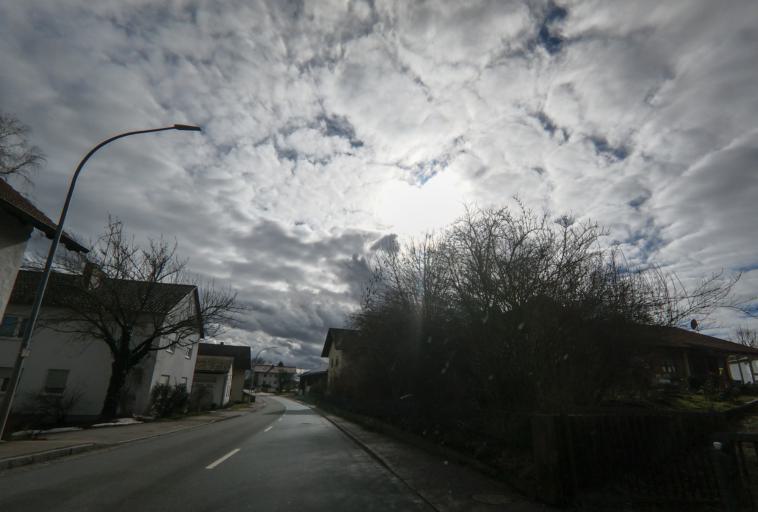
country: DE
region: Bavaria
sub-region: Lower Bavaria
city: Essenbach
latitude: 48.6391
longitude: 12.2104
